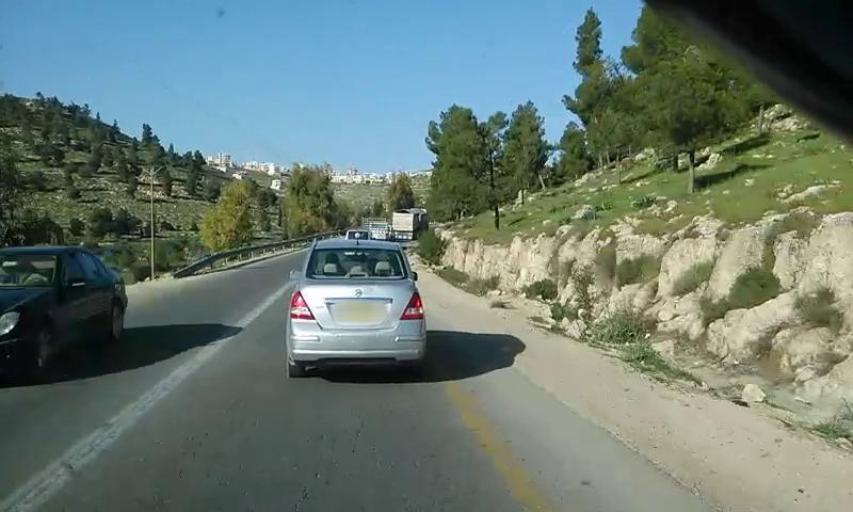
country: PS
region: West Bank
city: Ar Rihiyah
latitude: 31.4902
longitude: 35.0675
